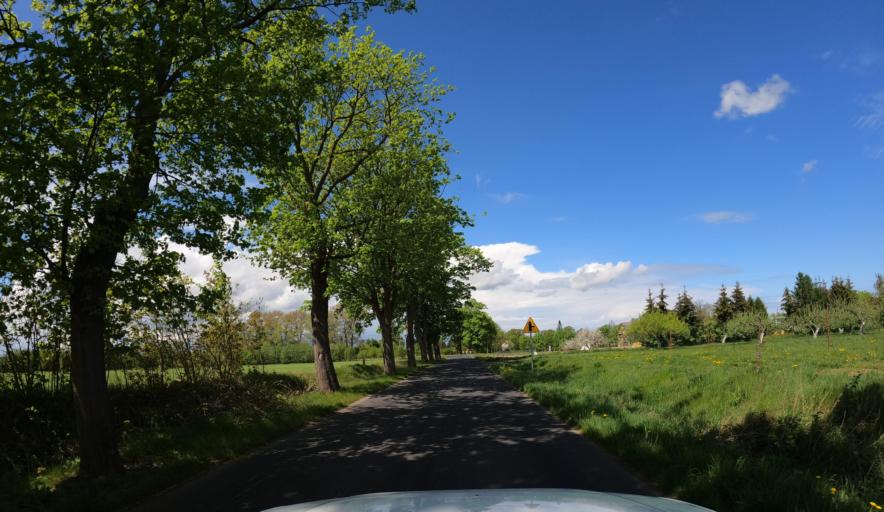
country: PL
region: West Pomeranian Voivodeship
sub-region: Powiat kamienski
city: Kamien Pomorski
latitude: 53.9178
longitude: 14.7071
